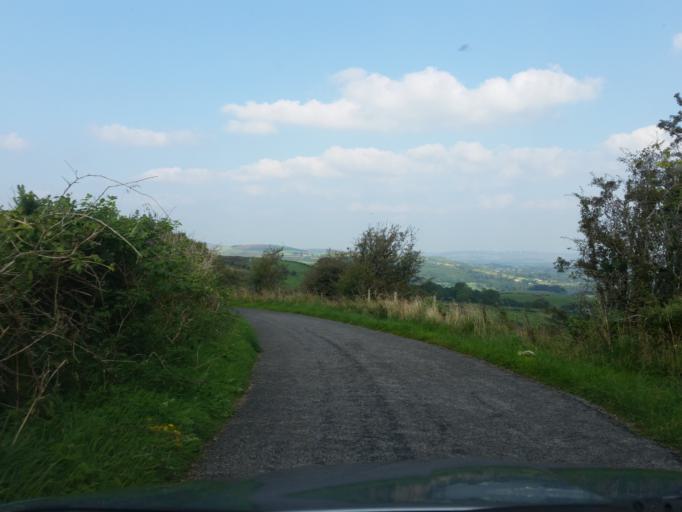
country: GB
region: Northern Ireland
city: Ballinamallard
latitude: 54.3486
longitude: -7.5200
